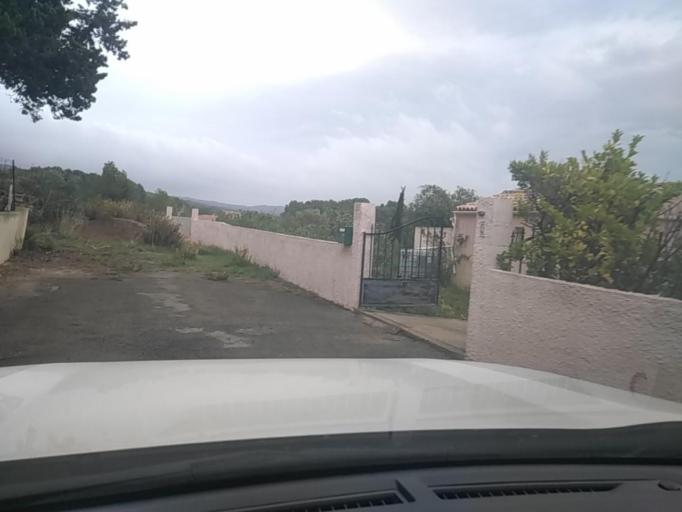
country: FR
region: Languedoc-Roussillon
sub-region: Departement de l'Herault
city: Olonzac
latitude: 43.3261
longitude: 2.7169
